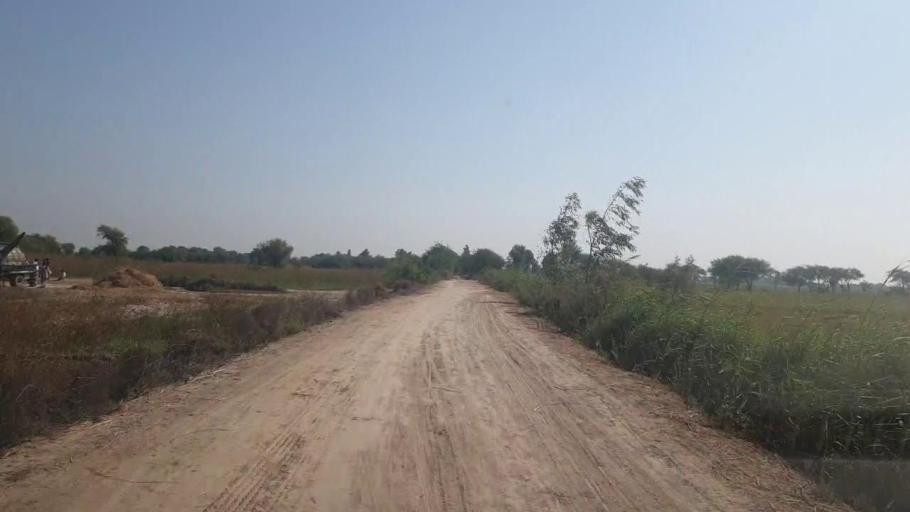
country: PK
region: Sindh
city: Badin
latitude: 24.7122
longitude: 68.8780
